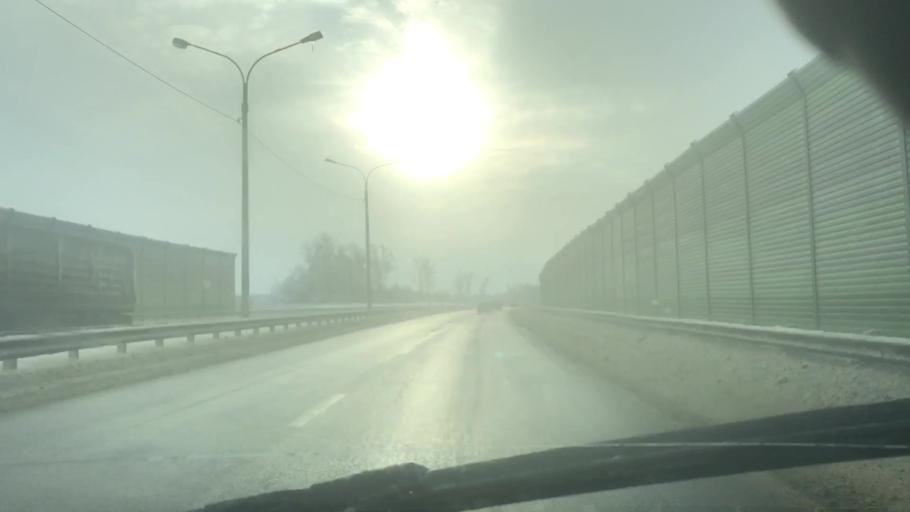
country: RU
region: Tula
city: Venev
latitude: 54.2757
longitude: 38.1602
